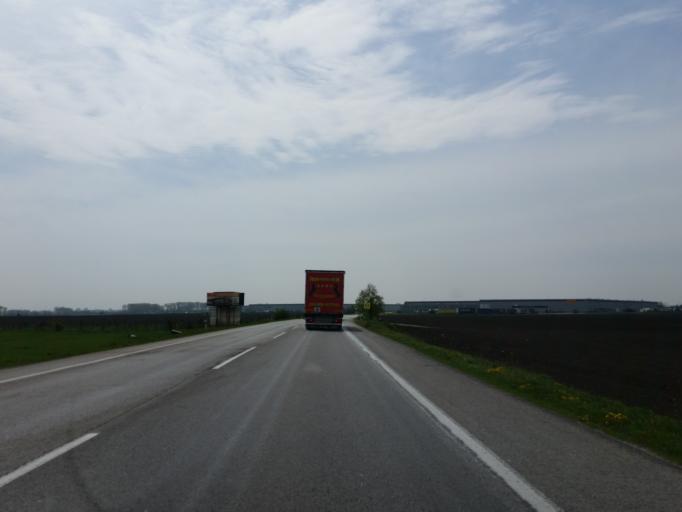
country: SK
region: Trnavsky
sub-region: Okres Galanta
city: Galanta
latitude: 48.2421
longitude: 17.7352
